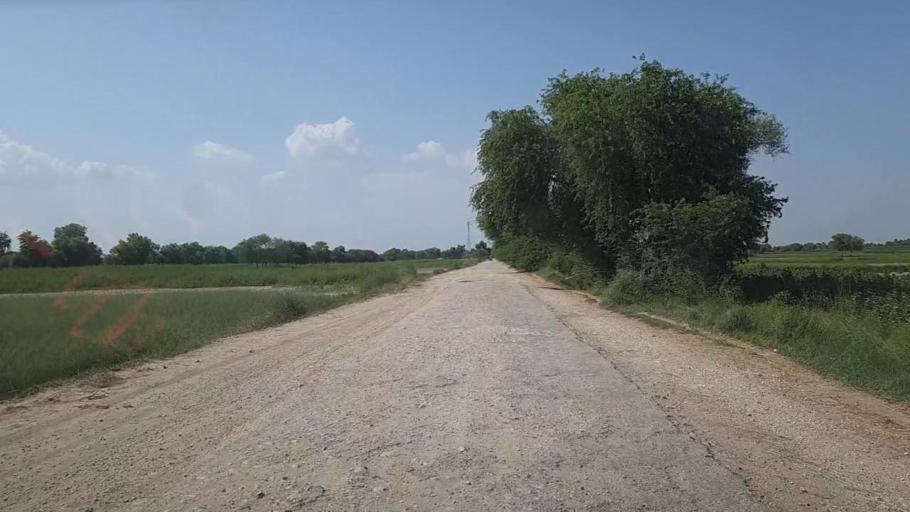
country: PK
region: Sindh
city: Khairpur
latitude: 28.1137
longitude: 69.6190
